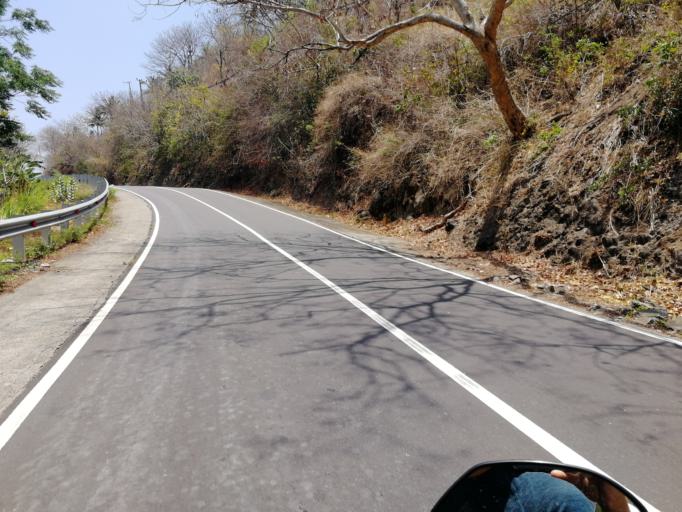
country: ID
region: West Nusa Tenggara
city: Karangsubagan
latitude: -8.4488
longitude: 116.0359
